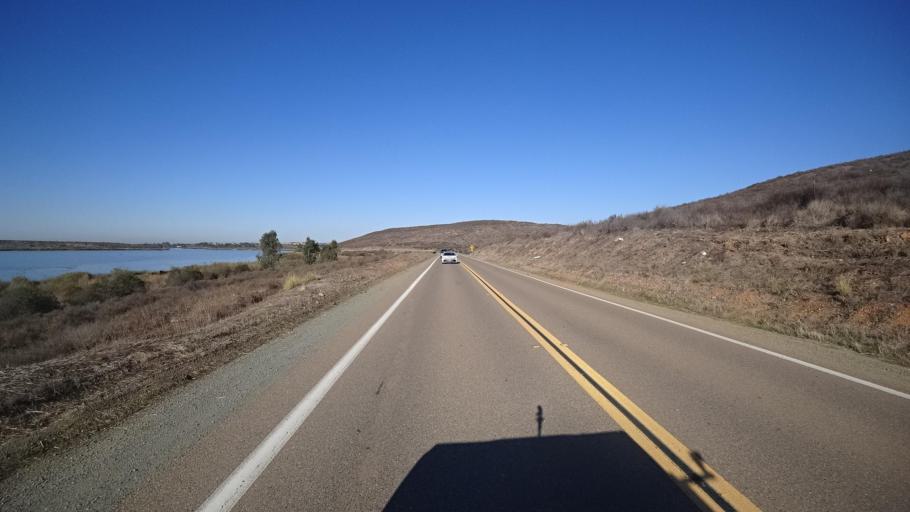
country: US
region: California
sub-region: San Diego County
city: Jamul
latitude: 32.6348
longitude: -116.9090
